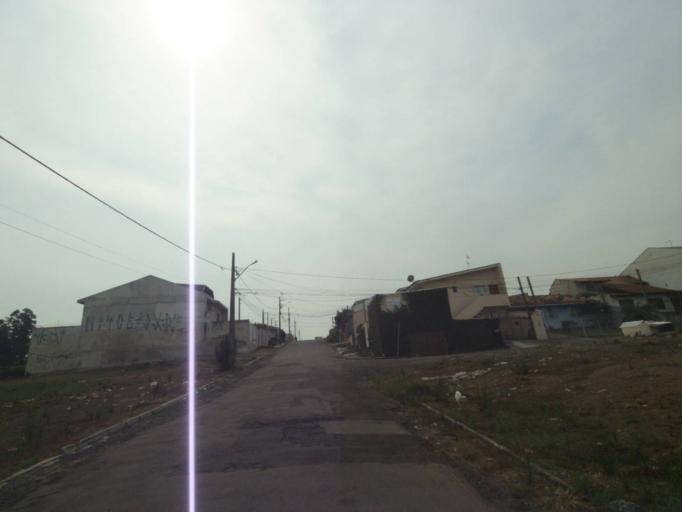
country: BR
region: Parana
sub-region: Sao Jose Dos Pinhais
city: Sao Jose dos Pinhais
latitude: -25.5303
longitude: -49.2785
